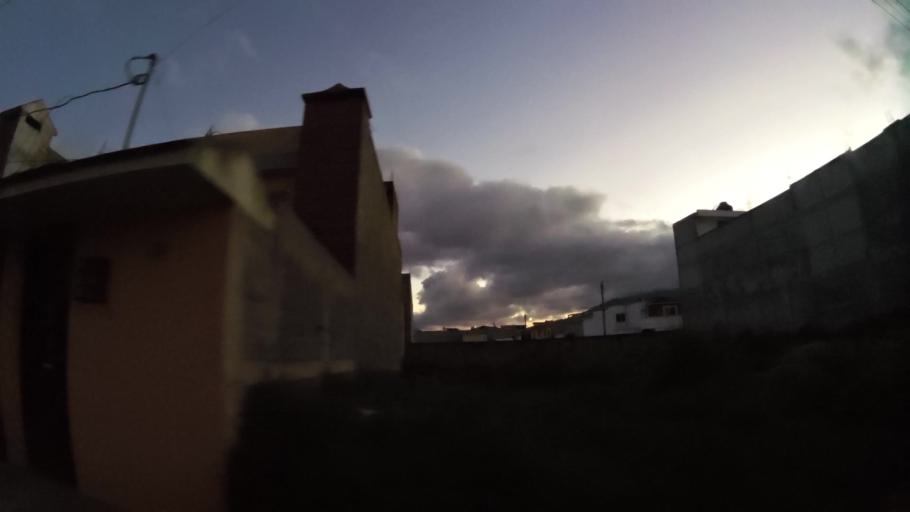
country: GT
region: Quetzaltenango
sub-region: Municipio de La Esperanza
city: La Esperanza
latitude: 14.8641
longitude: -91.5466
